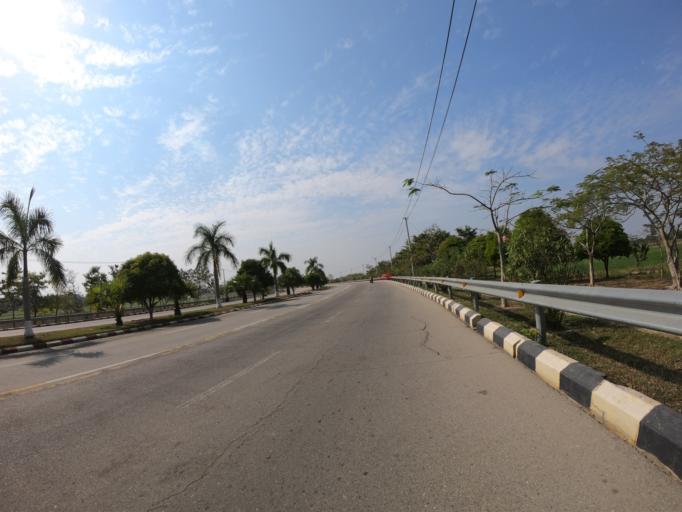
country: MM
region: Mandalay
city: Nay Pyi Taw
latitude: 19.6501
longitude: 96.1573
